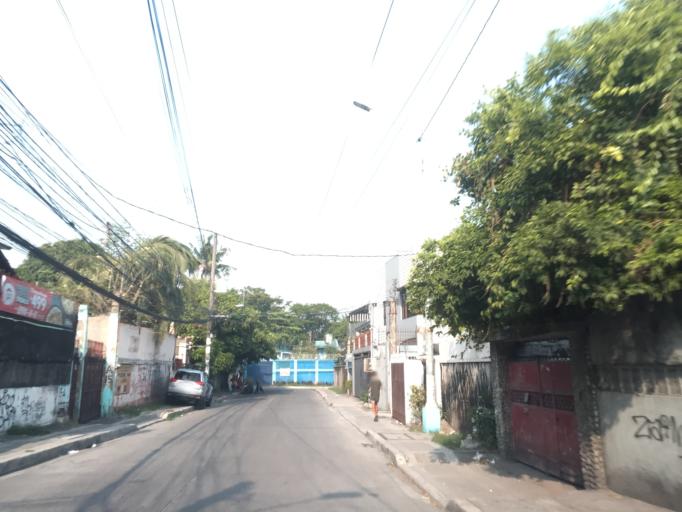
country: PH
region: Calabarzon
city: Bagong Pagasa
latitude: 14.6637
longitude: 121.0189
